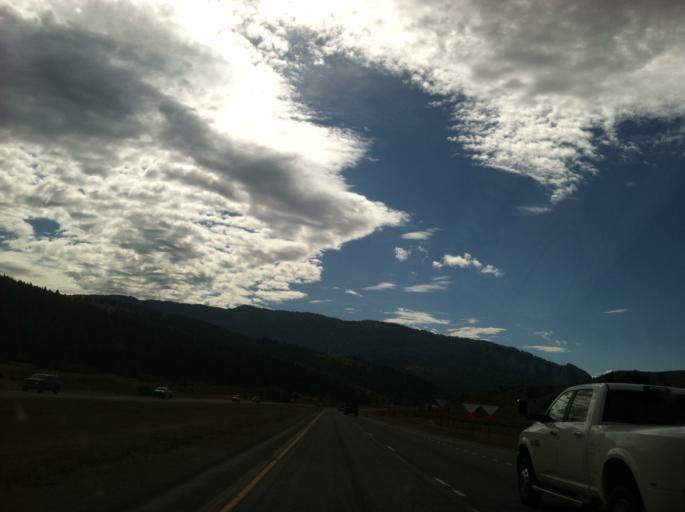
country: US
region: Montana
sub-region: Gallatin County
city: Bozeman
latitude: 45.6565
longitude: -110.8488
